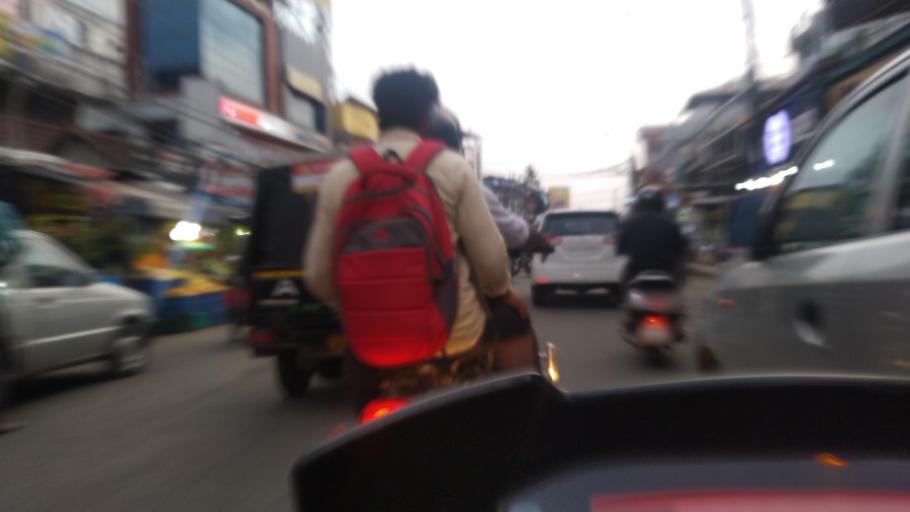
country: IN
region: Kerala
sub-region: Ernakulam
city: Elur
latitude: 10.0022
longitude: 76.3058
